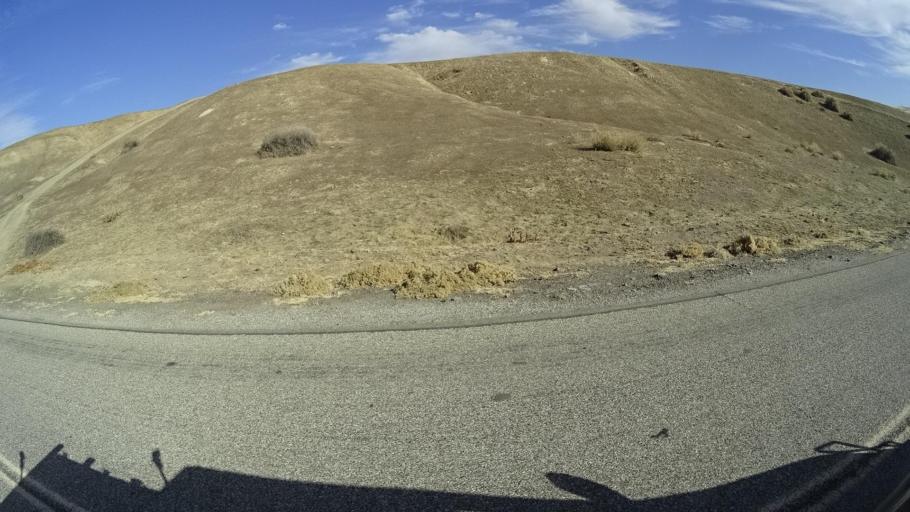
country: US
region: California
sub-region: Kern County
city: Oildale
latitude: 35.5184
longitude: -118.9281
